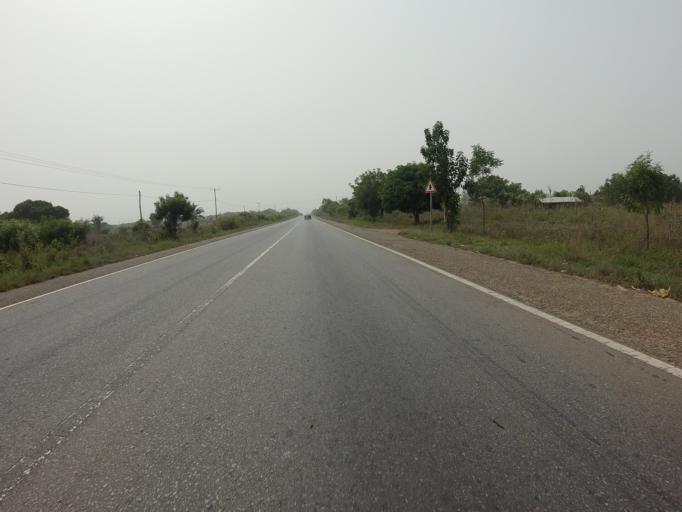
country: GH
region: Volta
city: Anloga
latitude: 5.9531
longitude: 0.5241
